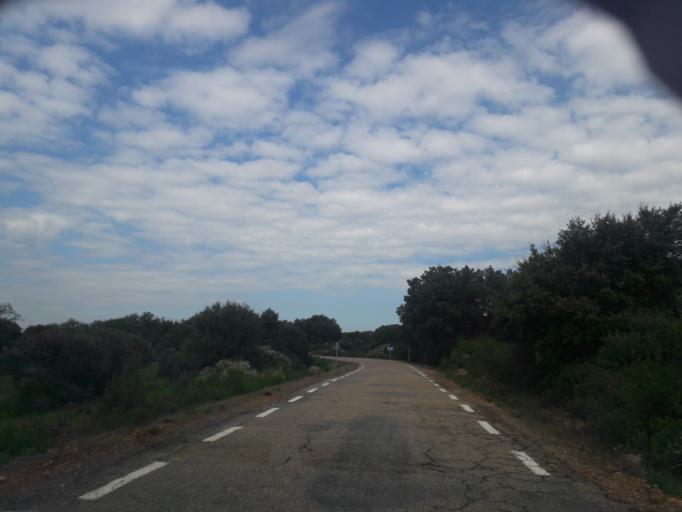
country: ES
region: Castille and Leon
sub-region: Provincia de Salamanca
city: Serradilla del Arroyo
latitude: 40.5394
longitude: -6.3850
